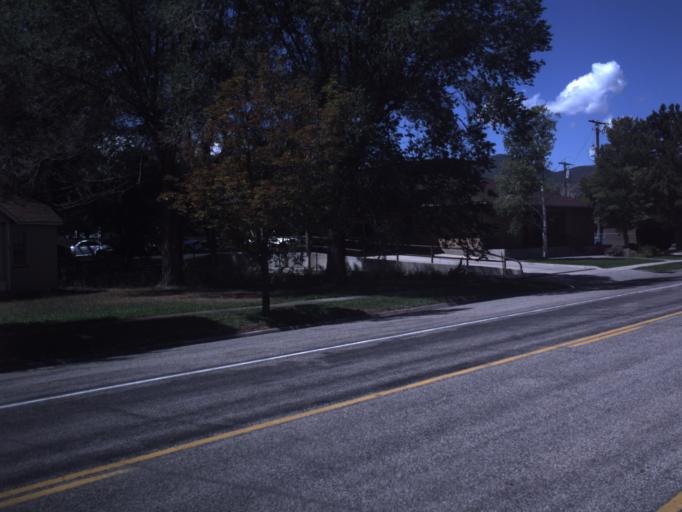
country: US
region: Utah
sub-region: Piute County
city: Junction
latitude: 38.1718
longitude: -112.2746
